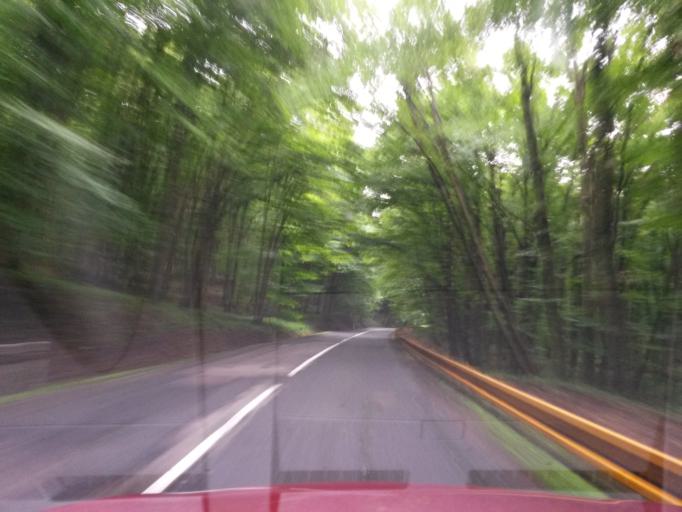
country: SK
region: Nitriansky
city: Sahy
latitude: 48.1937
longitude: 19.0572
